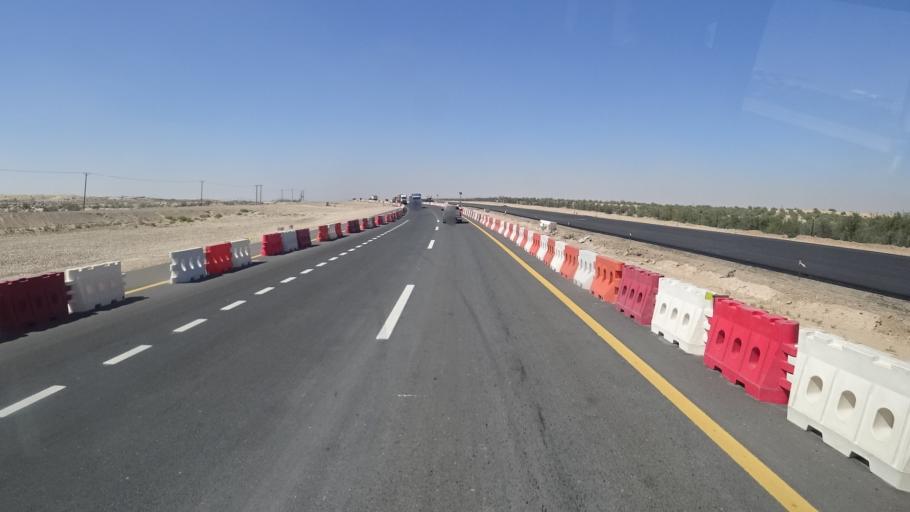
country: AE
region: Abu Dhabi
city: Abu Dhabi
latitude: 24.2043
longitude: 54.8536
